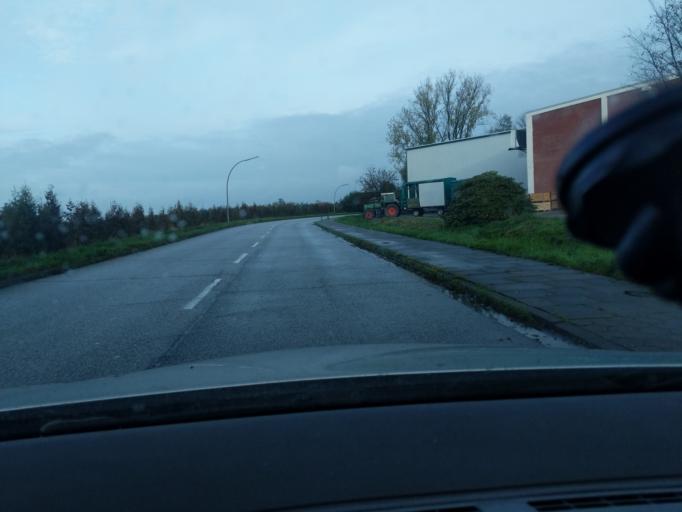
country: DE
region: Lower Saxony
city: Neu Wulmstorf
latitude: 53.5195
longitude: 9.7805
